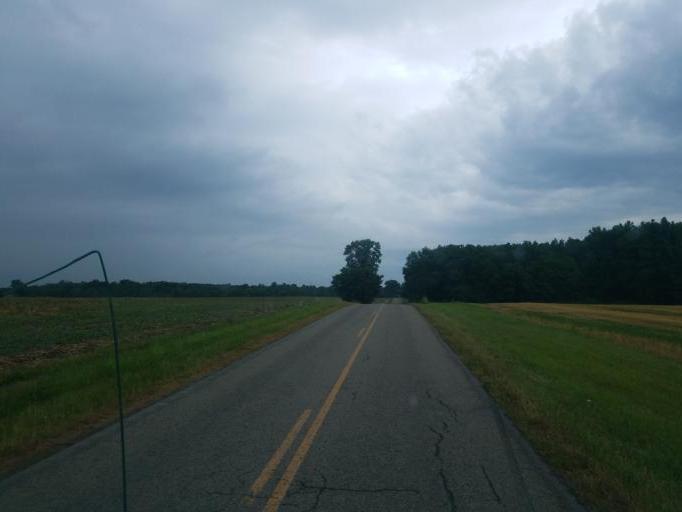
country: US
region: Ohio
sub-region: Defiance County
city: Hicksville
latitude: 41.3293
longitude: -84.8040
